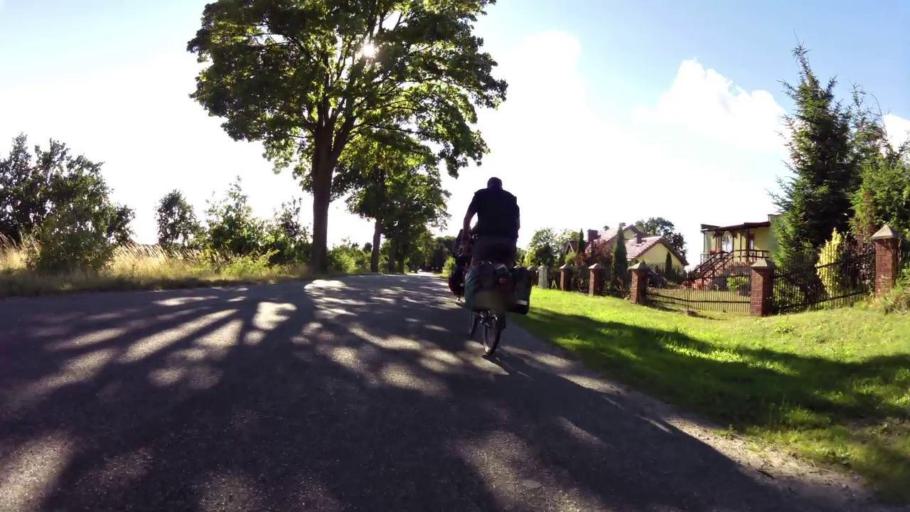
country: PL
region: West Pomeranian Voivodeship
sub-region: Powiat swidwinski
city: Swidwin
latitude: 53.7750
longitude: 15.7505
